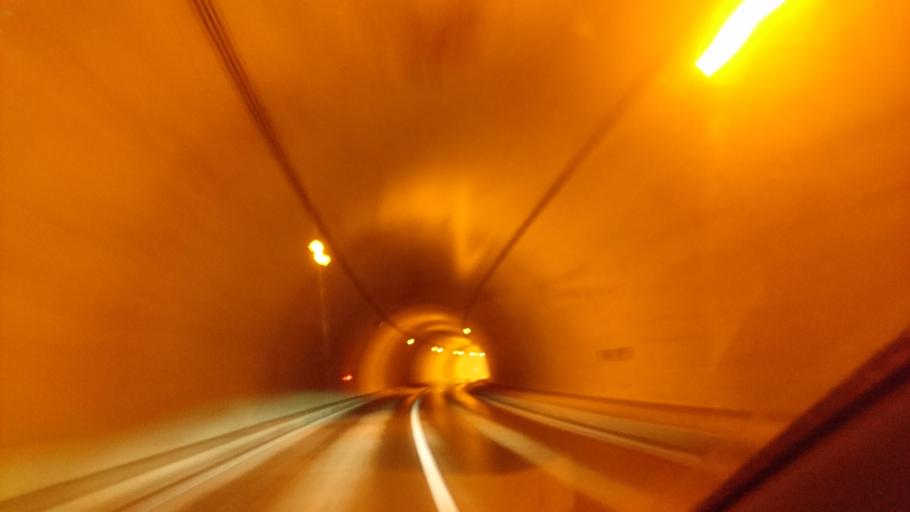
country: JP
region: Iwate
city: Mizusawa
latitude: 39.1265
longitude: 140.9312
